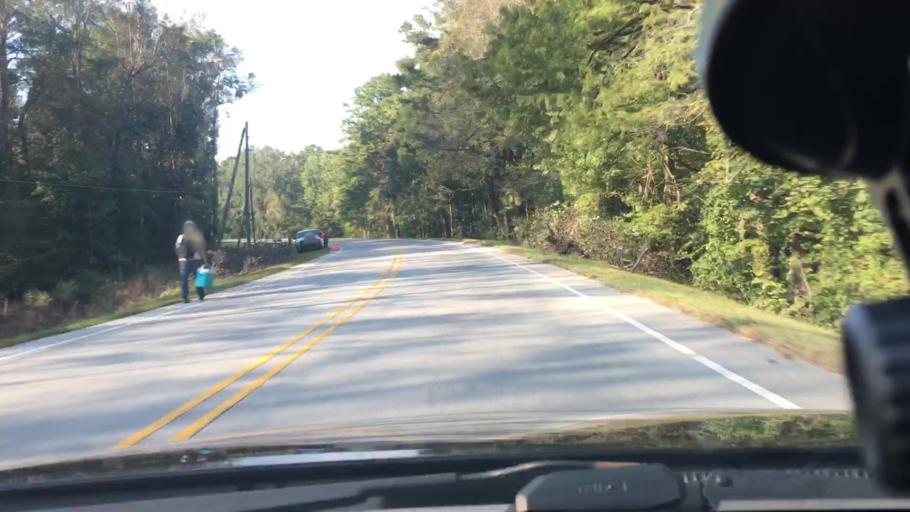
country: US
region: North Carolina
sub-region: Craven County
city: Vanceboro
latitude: 35.2340
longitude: -77.0729
